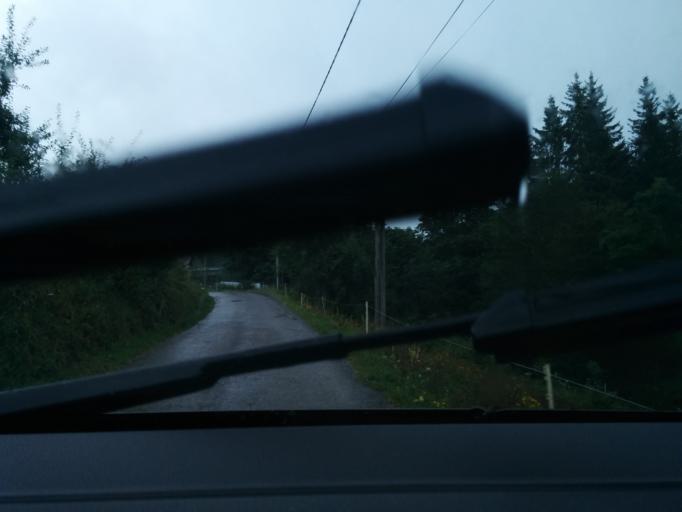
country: FR
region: Franche-Comte
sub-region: Departement du Jura
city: Valfin-les-Saint-Claude
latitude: 46.4646
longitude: 5.8369
